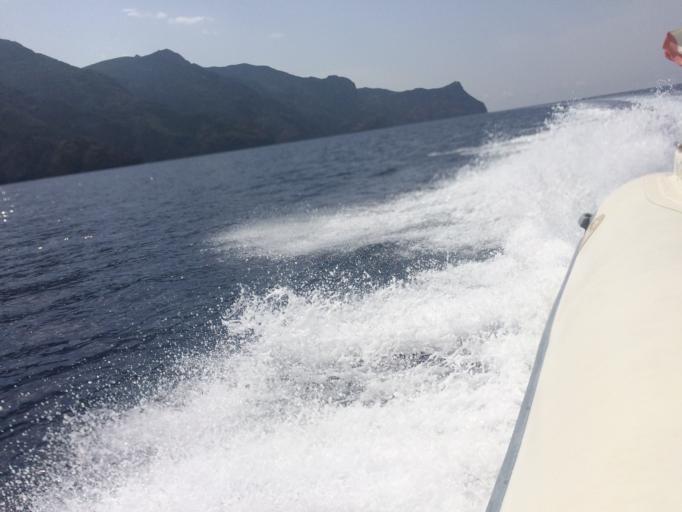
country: IT
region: Tuscany
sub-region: Provincia di Livorno
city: Capraia Isola
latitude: 43.0496
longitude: 9.7938
